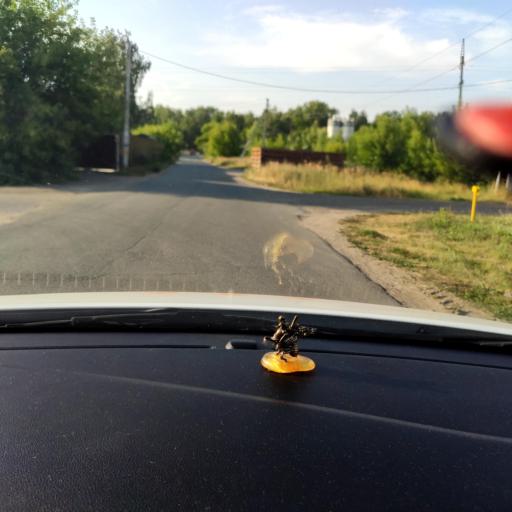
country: RU
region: Tatarstan
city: Staroye Arakchino
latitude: 55.8108
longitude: 48.9134
